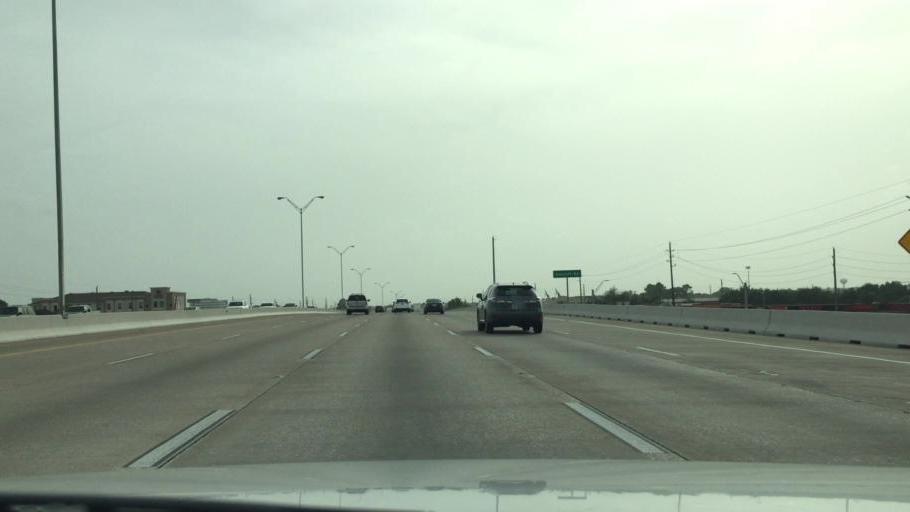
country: US
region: Texas
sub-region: Harris County
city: Jersey Village
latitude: 29.9305
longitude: -95.5432
